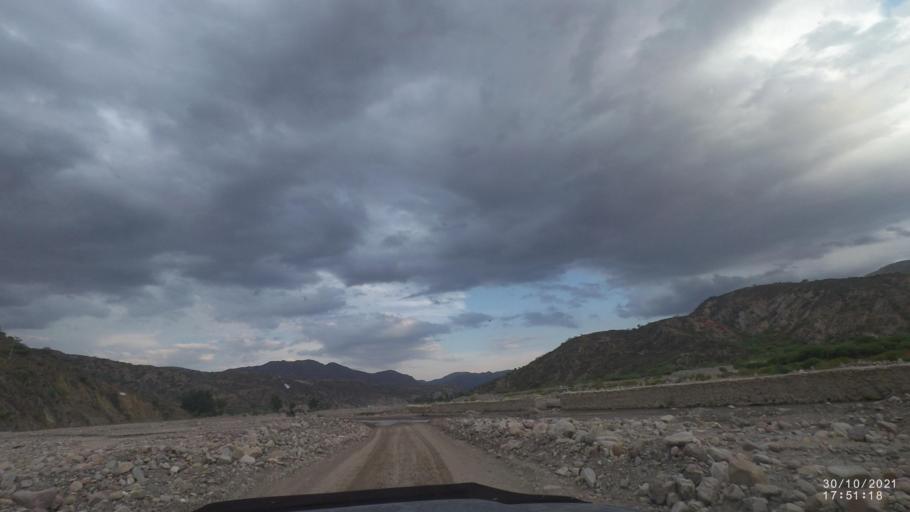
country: BO
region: Cochabamba
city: Sipe Sipe
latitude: -17.5365
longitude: -66.5053
